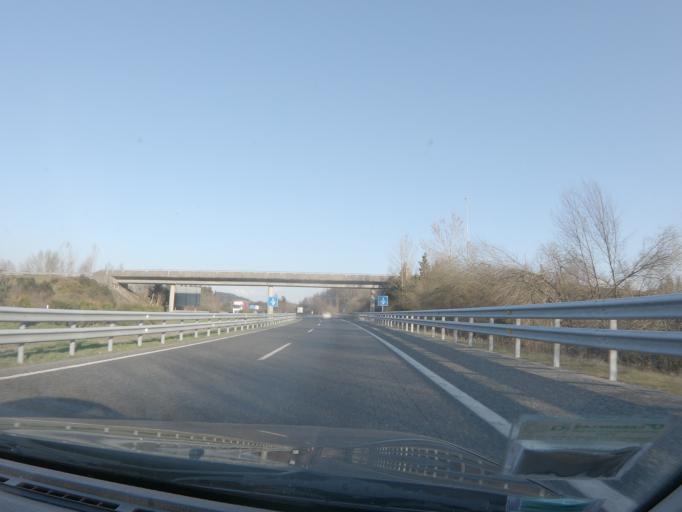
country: ES
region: Galicia
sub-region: Provincia de Lugo
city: O Paramo
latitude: 42.9065
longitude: -7.3004
